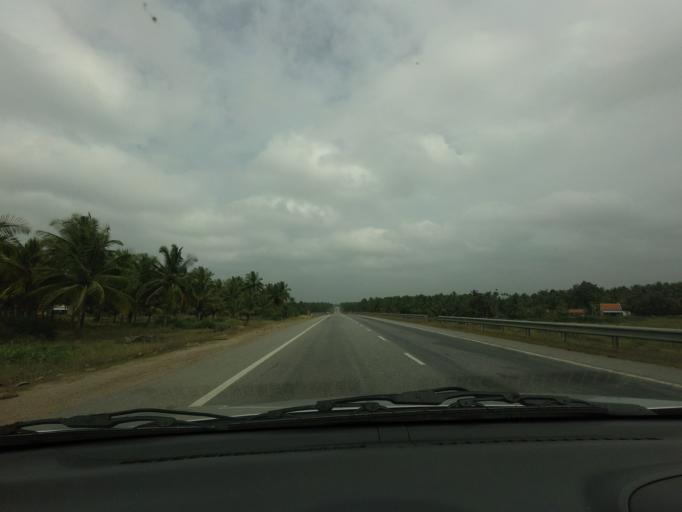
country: IN
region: Karnataka
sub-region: Hassan
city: Channarayapatna
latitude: 12.9195
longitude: 76.4133
